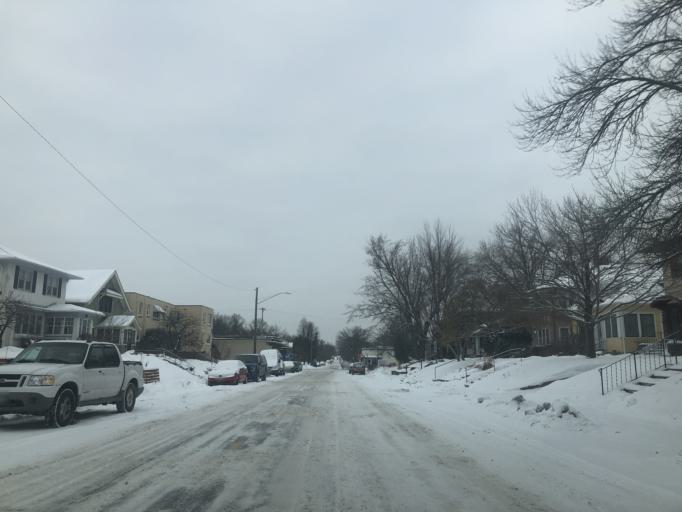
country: US
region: Minnesota
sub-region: Hennepin County
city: Richfield
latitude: 44.9184
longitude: -93.2909
